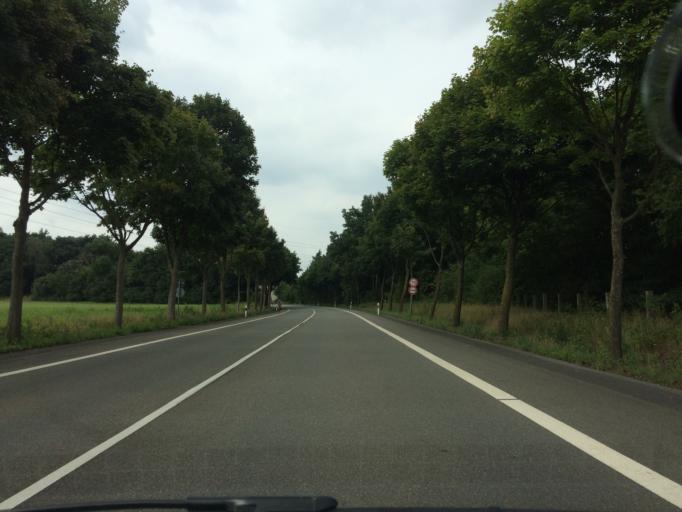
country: DE
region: North Rhine-Westphalia
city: Marl
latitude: 51.7066
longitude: 7.0656
